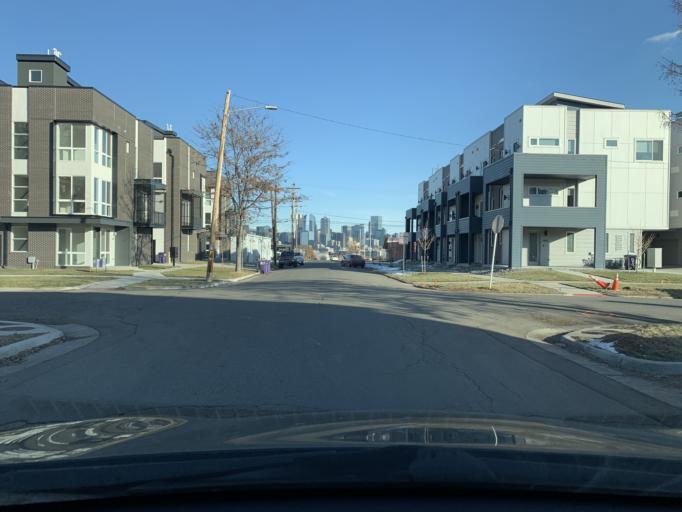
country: US
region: Colorado
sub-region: Jefferson County
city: Edgewater
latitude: 39.7464
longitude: -105.0271
